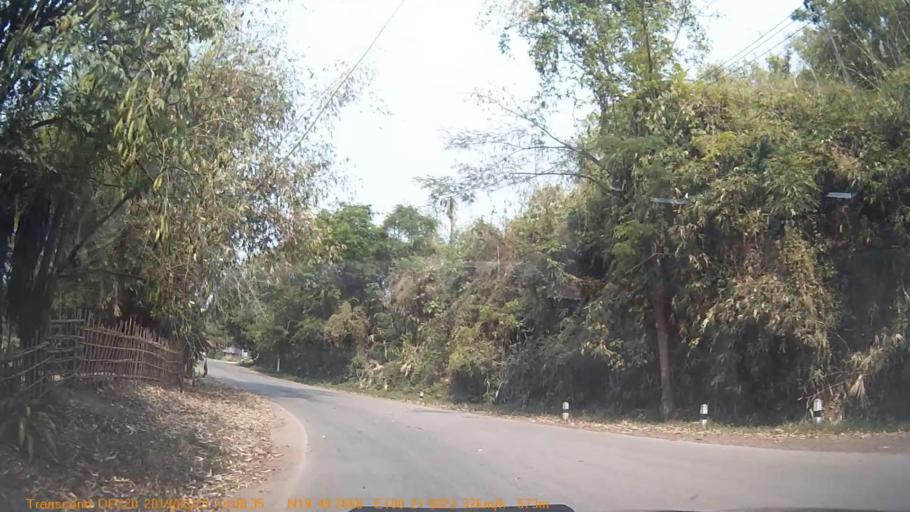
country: TH
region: Chiang Rai
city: Khun Tan
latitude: 19.8212
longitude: 100.3665
